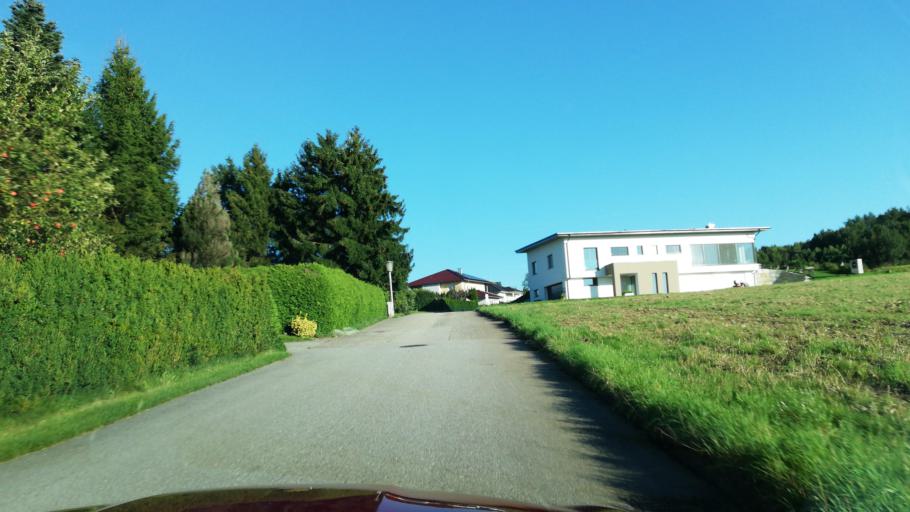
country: AT
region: Upper Austria
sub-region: Politischer Bezirk Ried im Innkreis
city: Ried im Innkreis
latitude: 48.2456
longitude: 13.4510
